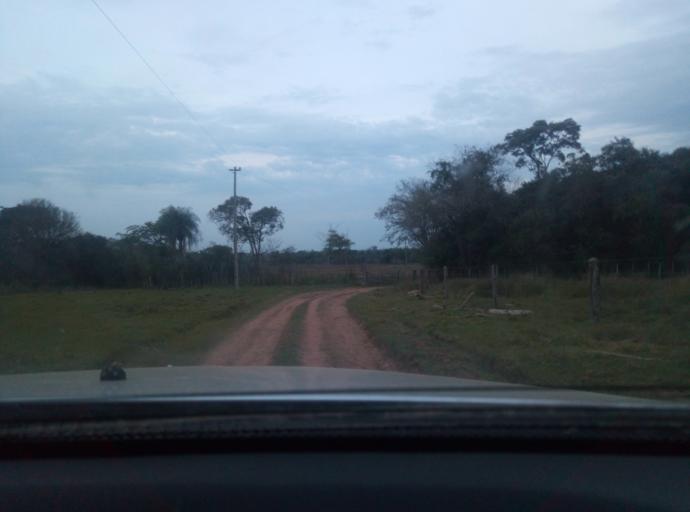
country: PY
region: Caaguazu
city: Carayao
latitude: -25.1468
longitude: -56.3823
